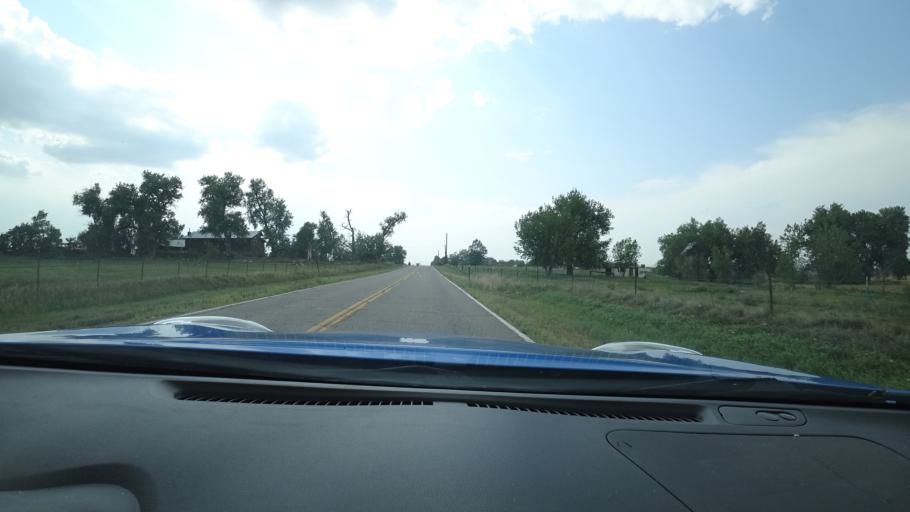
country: US
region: Colorado
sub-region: Adams County
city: Brighton
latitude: 39.9216
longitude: -104.8300
